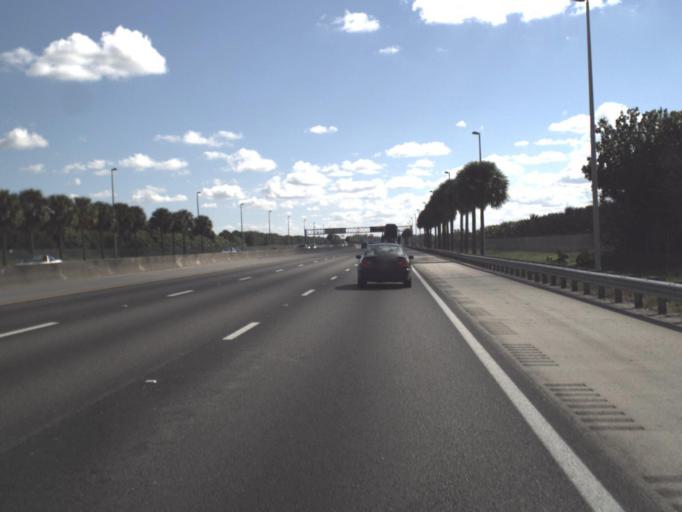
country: US
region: Florida
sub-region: Palm Beach County
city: Villages of Oriole
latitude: 26.5031
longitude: -80.1727
